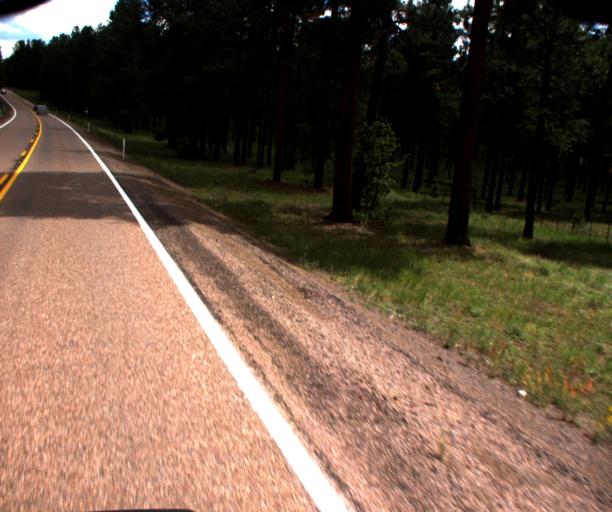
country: US
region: Arizona
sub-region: Navajo County
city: Pinetop-Lakeside
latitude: 34.0650
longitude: -109.7757
